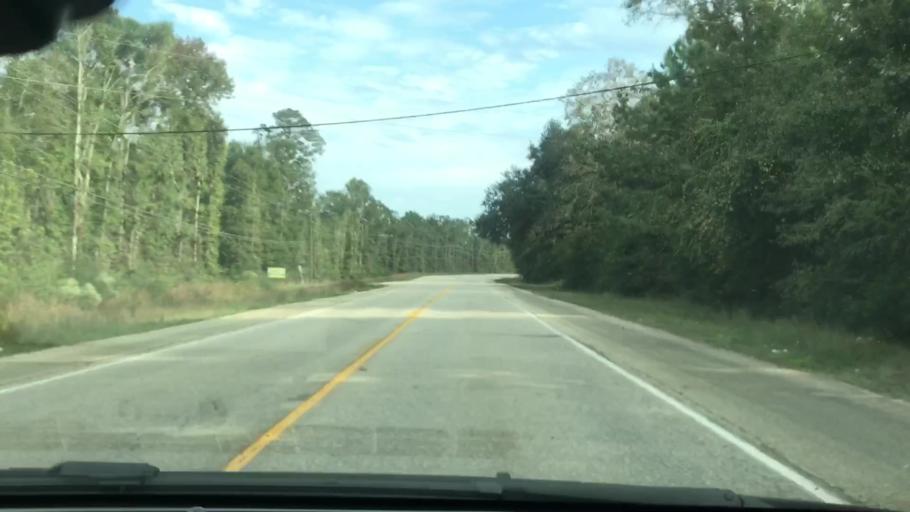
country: US
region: Mississippi
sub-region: Pearl River County
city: Nicholson
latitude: 30.5325
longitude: -89.8643
